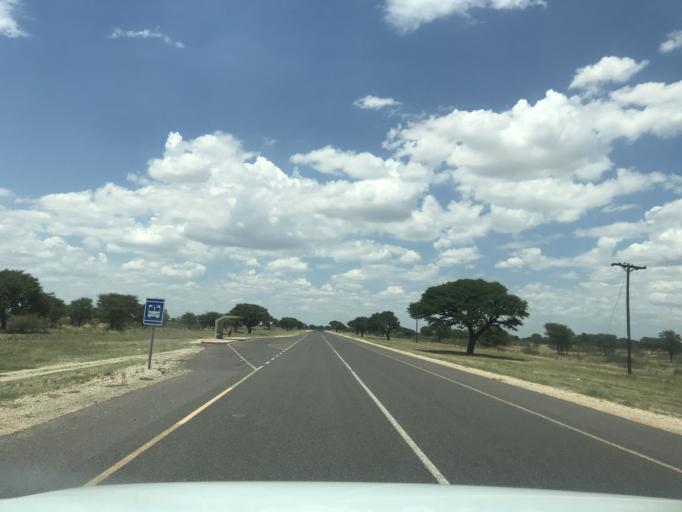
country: BW
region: South East
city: Janeng
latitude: -25.6411
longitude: 25.1509
